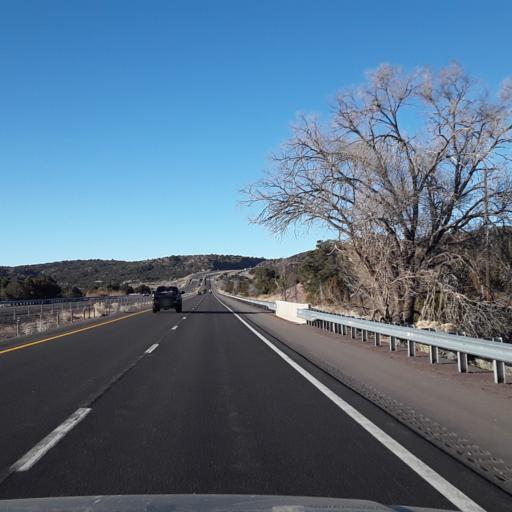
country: US
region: New Mexico
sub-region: Santa Fe County
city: Eldorado at Santa Fe
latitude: 35.5434
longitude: -105.8380
